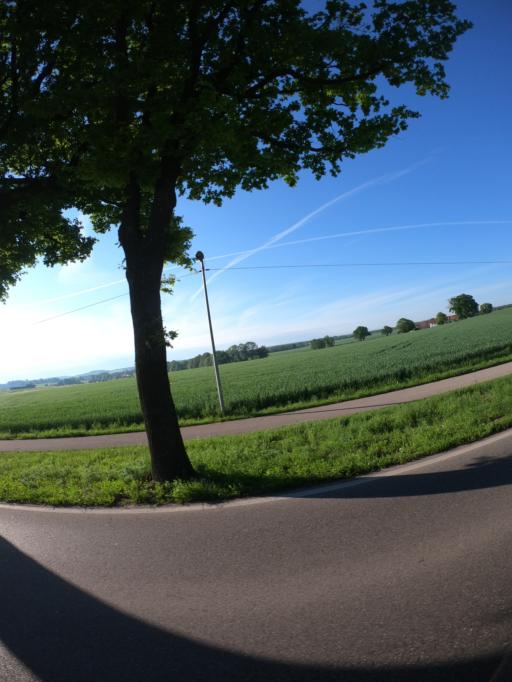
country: DE
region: Bavaria
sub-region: Upper Bavaria
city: Erding
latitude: 48.3096
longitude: 11.9455
